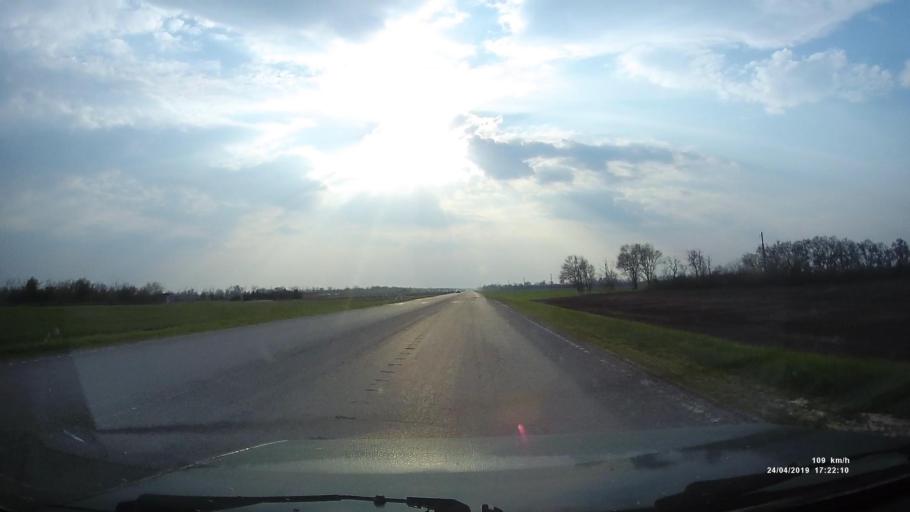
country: RU
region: Rostov
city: Gigant
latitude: 46.5201
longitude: 41.3156
